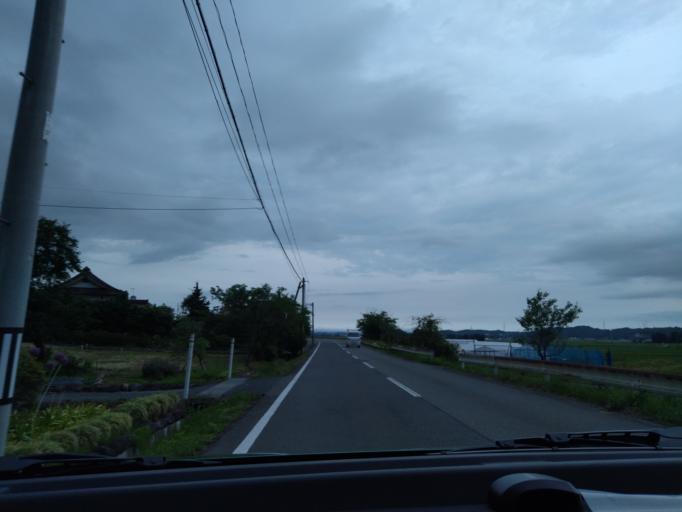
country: JP
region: Iwate
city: Ichinoseki
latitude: 38.8236
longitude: 140.9402
